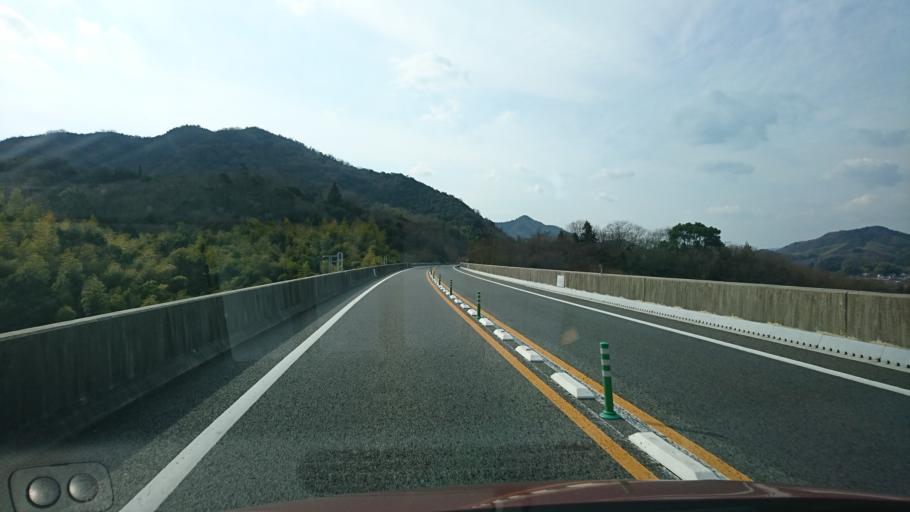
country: JP
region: Hiroshima
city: Innoshima
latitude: 34.1356
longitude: 133.0519
